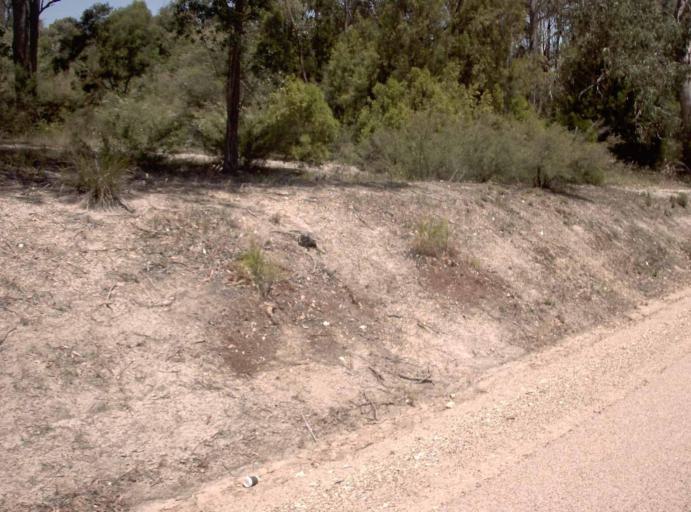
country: AU
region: Victoria
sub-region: East Gippsland
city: Bairnsdale
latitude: -37.7470
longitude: 147.7566
